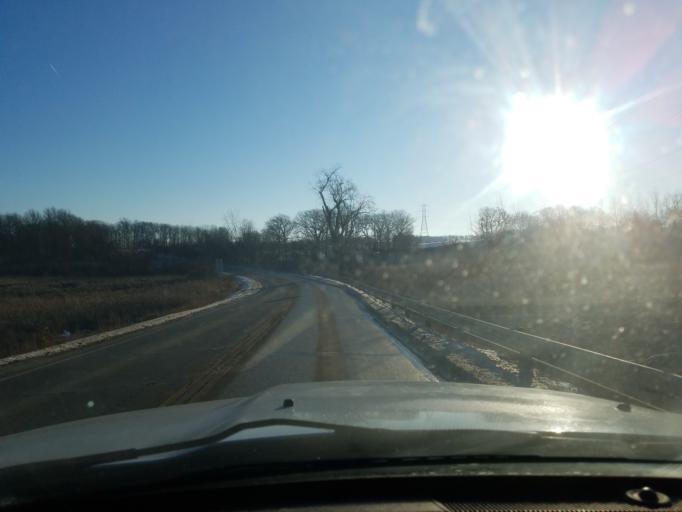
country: US
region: Indiana
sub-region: Noble County
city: Ligonier
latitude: 41.4508
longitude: -85.5816
